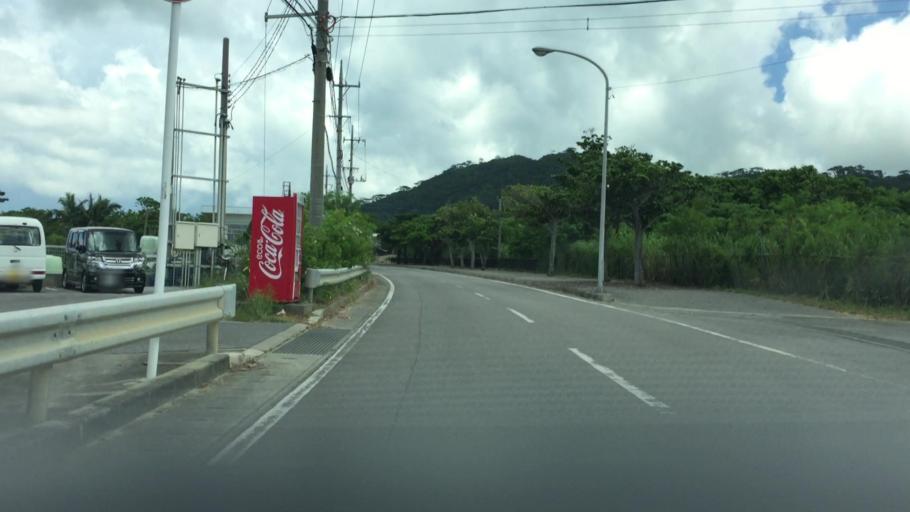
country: JP
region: Okinawa
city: Ishigaki
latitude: 24.3624
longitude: 124.1430
